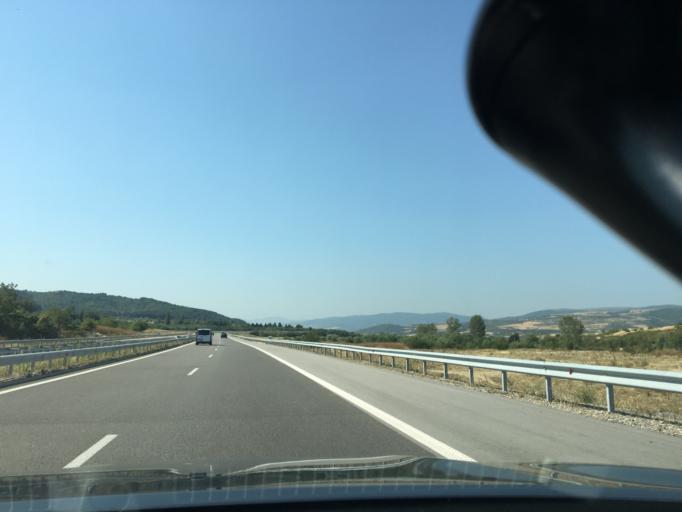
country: BG
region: Kyustendil
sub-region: Obshtina Dupnitsa
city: Dupnitsa
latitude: 42.2218
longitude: 23.0765
